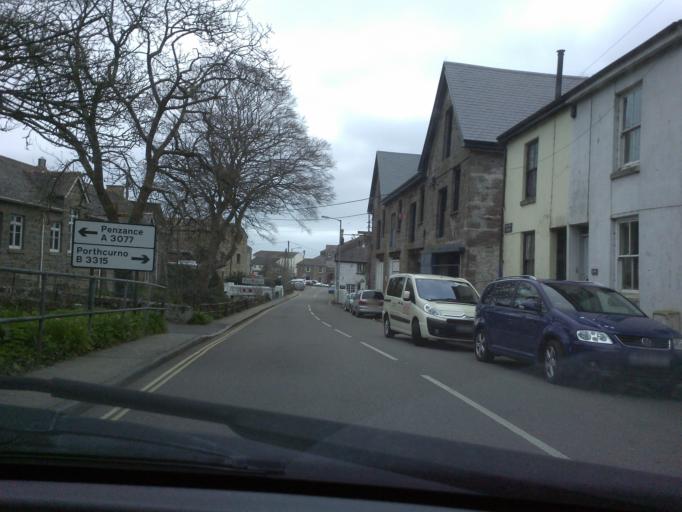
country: GB
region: England
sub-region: Cornwall
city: Penzance
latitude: 50.1073
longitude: -5.5520
